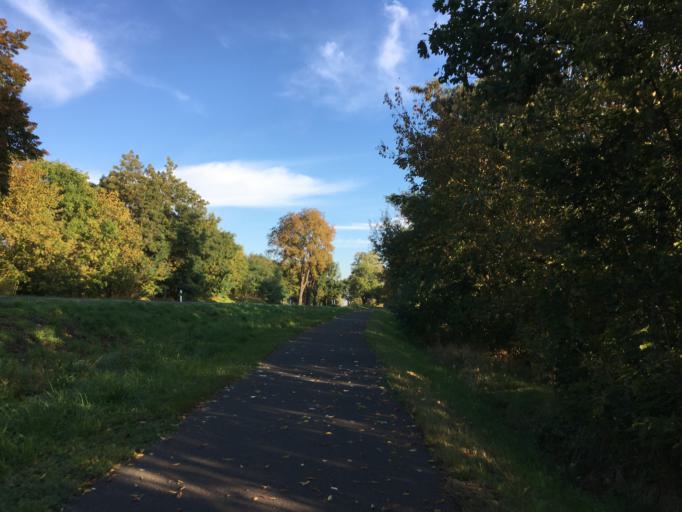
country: DE
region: Brandenburg
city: Lebus
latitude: 52.3900
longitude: 14.5176
